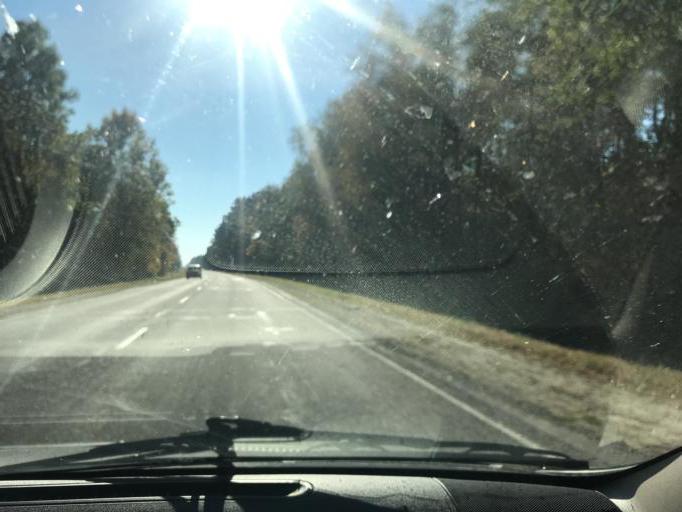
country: BY
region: Brest
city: Mikashevichy
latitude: 52.2849
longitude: 27.4420
